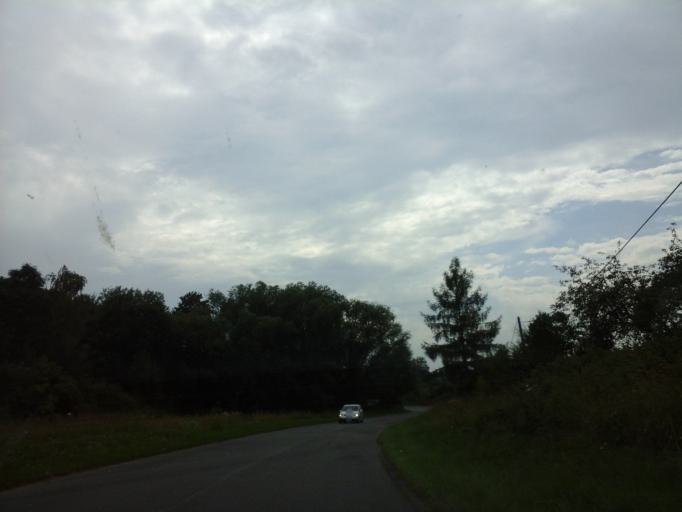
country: PL
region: Lower Silesian Voivodeship
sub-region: Powiat zabkowicki
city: Zabkowice Slaskie
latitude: 50.6032
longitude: 16.8260
